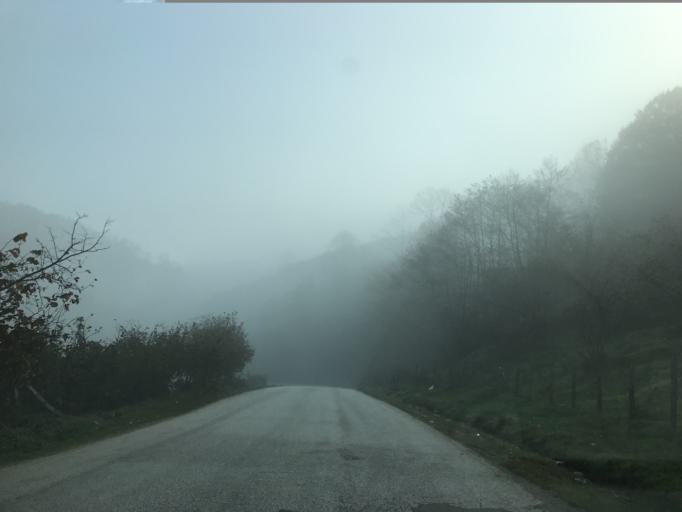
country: TR
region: Duzce
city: Cumayeri
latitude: 40.9001
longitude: 30.9530
